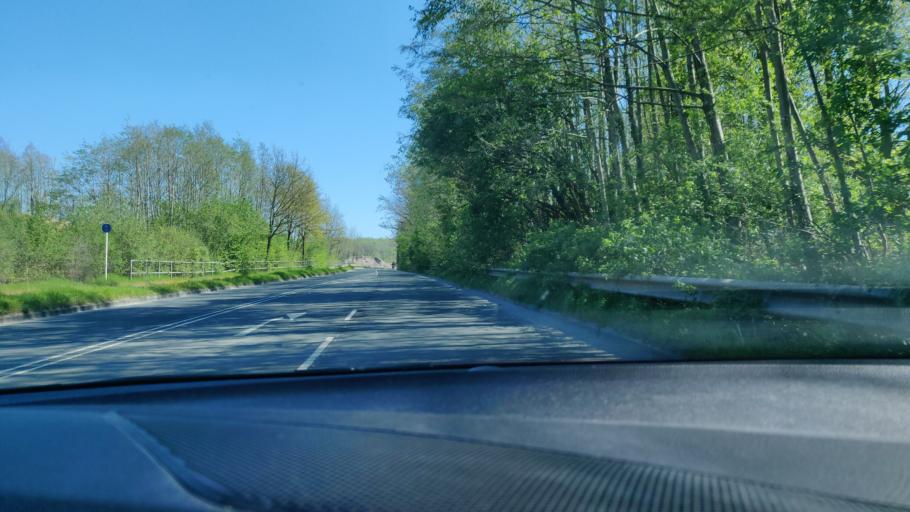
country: DE
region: North Rhine-Westphalia
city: Wulfrath
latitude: 51.2529
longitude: 7.0534
